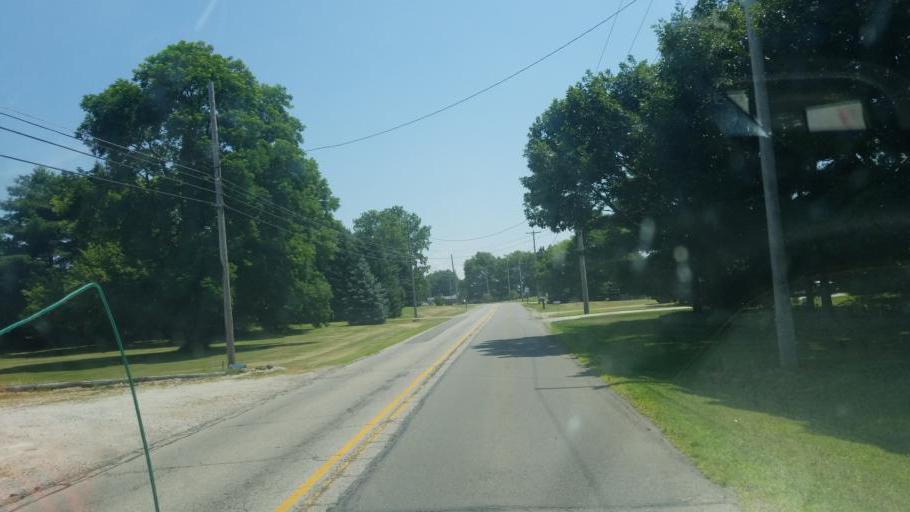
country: US
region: Ohio
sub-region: Richland County
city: Shelby
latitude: 40.8679
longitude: -82.6576
